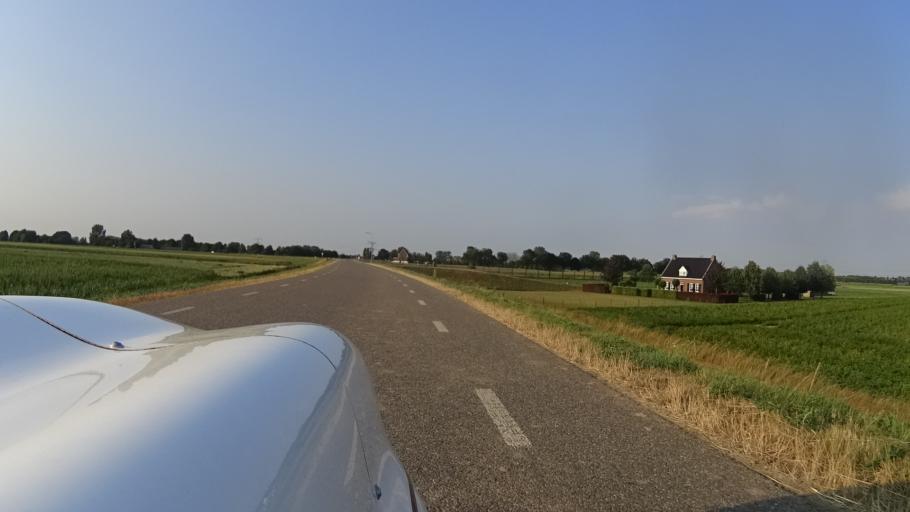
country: NL
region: Gelderland
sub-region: Gemeente Wijchen
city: Bergharen
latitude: 51.8077
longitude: 5.6577
